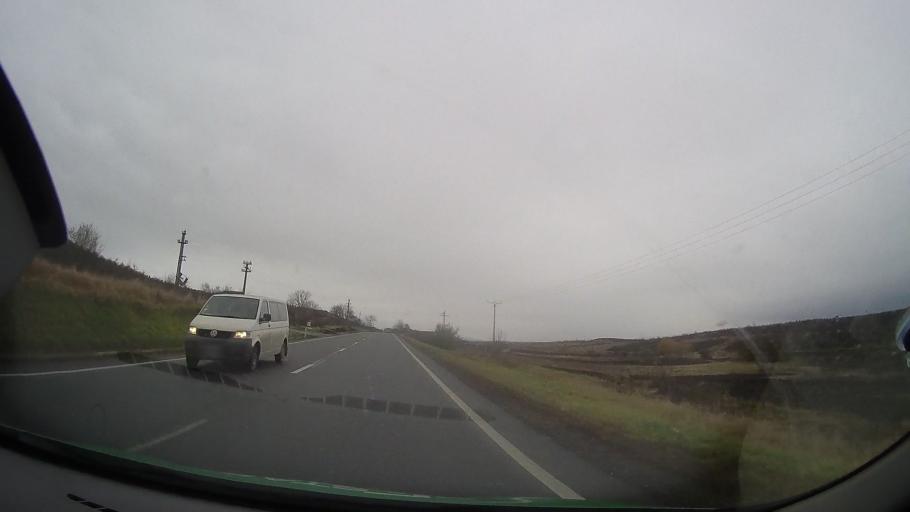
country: RO
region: Mures
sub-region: Comuna Breaza
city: Breaza
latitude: 46.7767
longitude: 24.6561
